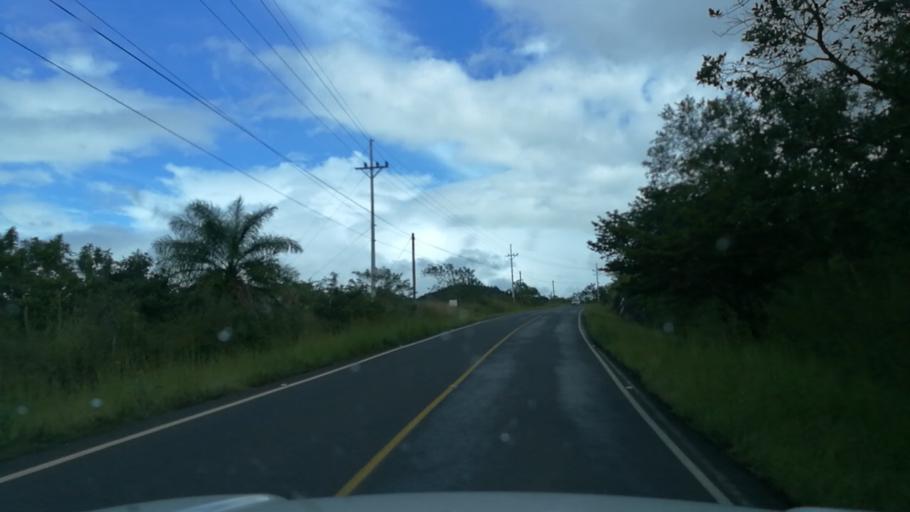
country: CR
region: Guanacaste
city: Fortuna
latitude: 10.6302
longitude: -85.2319
